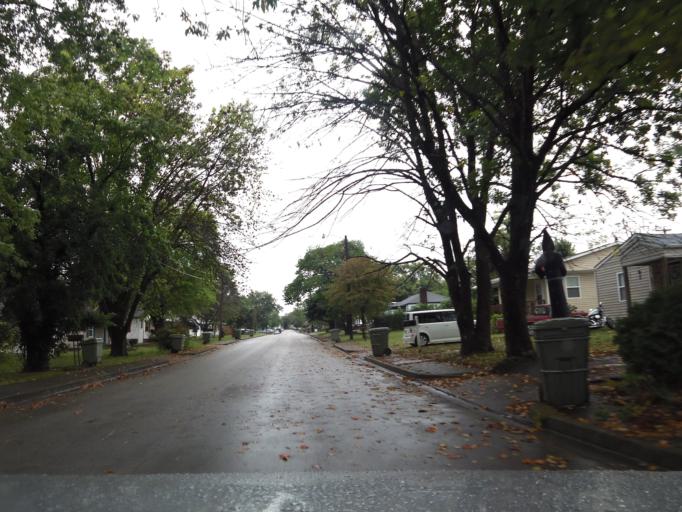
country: US
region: Tennessee
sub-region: Blount County
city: Maryville
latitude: 35.7721
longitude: -83.9600
